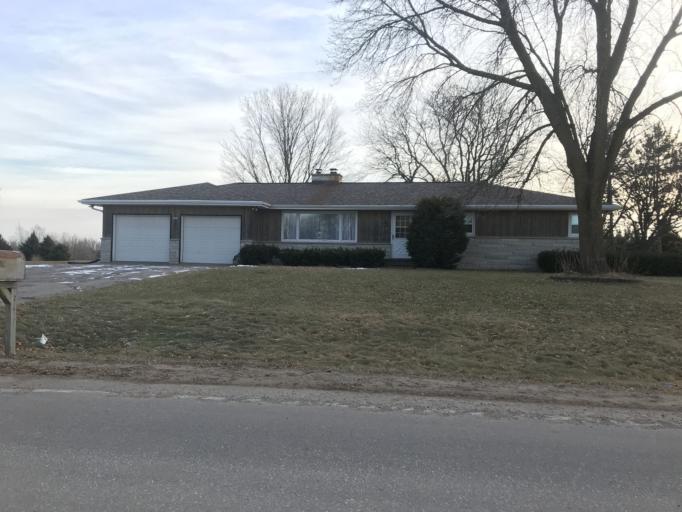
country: US
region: Wisconsin
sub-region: Oconto County
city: Oconto Falls
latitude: 45.0942
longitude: -88.0430
